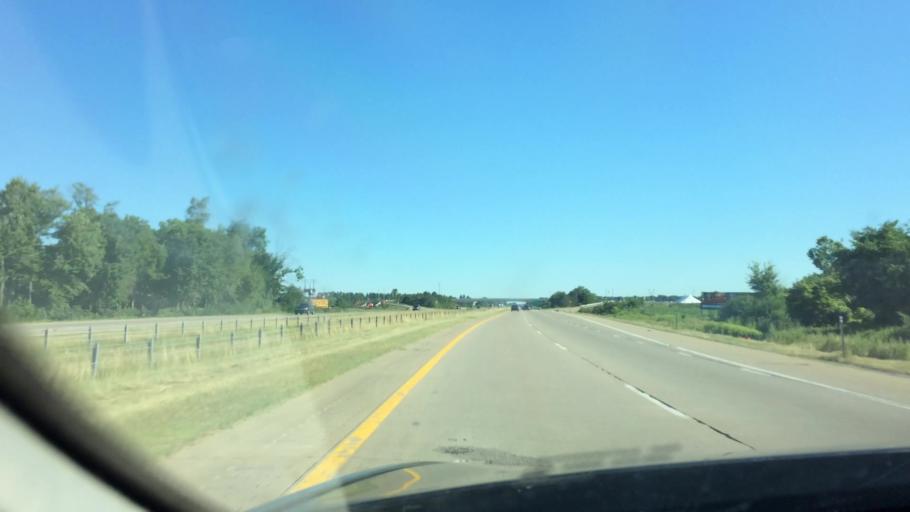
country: US
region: Ohio
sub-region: Lucas County
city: Sylvania
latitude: 41.7420
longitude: -83.6937
